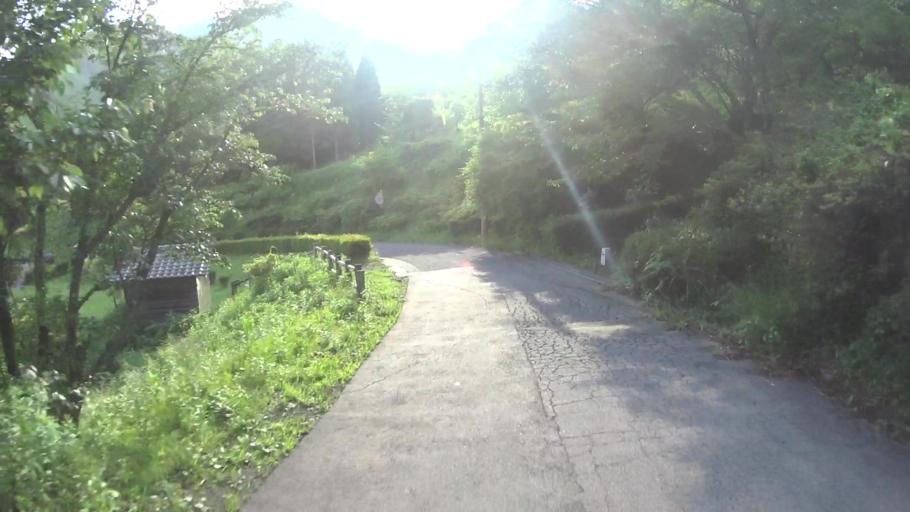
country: JP
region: Kumamoto
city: Aso
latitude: 32.9560
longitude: 131.0051
